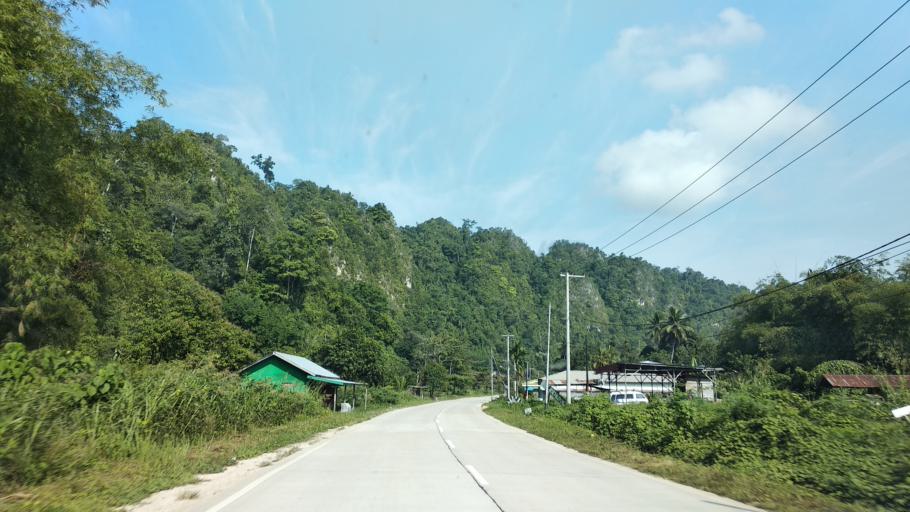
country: ID
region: East Kalimantan
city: Muarakomam
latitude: -1.7031
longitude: 115.8191
